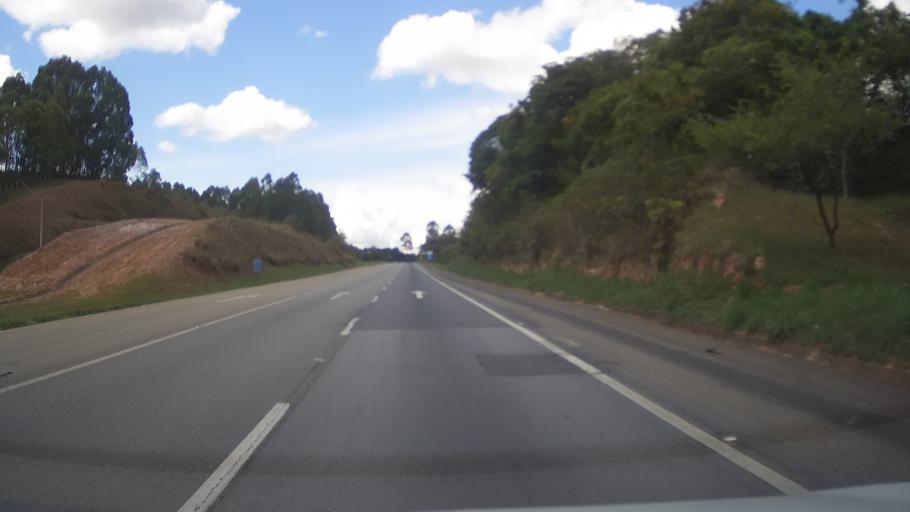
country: BR
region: Minas Gerais
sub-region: Santo Antonio Do Amparo
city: Santo Antonio do Amparo
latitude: -20.8523
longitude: -44.8356
